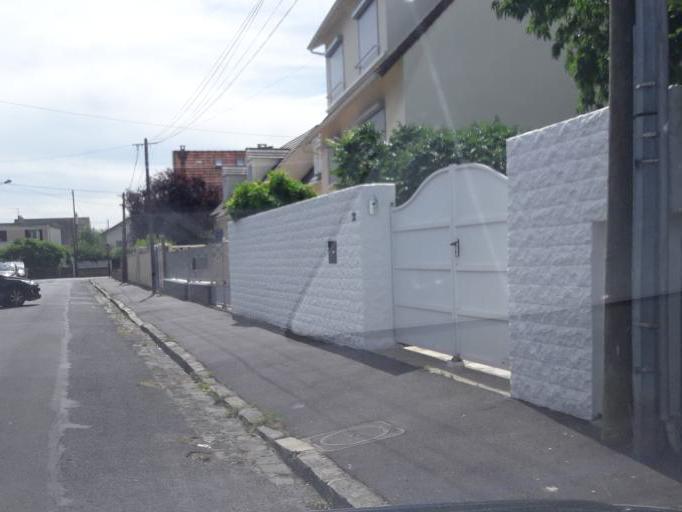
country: FR
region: Ile-de-France
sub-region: Departement de l'Essonne
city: Sainte-Genevieve-des-Bois
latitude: 48.6385
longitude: 2.3273
